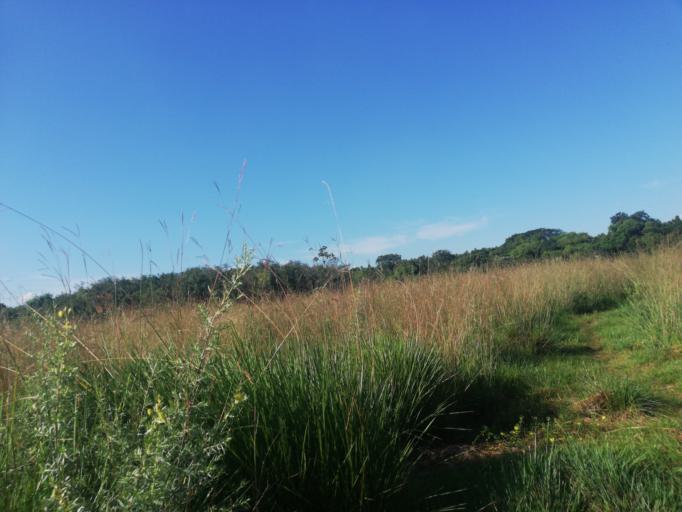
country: AR
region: Corrientes
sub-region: Departamento de San Miguel
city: San Miguel
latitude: -27.9899
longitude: -57.5419
